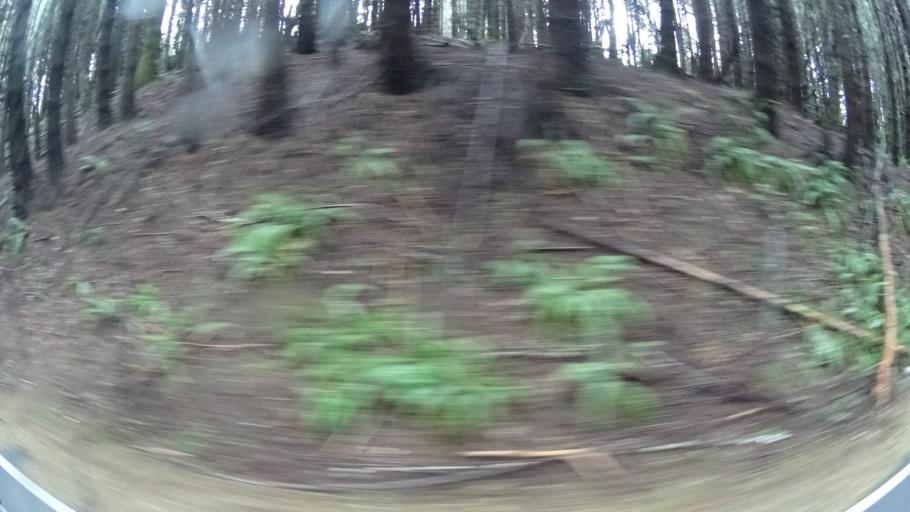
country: US
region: California
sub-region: Humboldt County
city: Westhaven-Moonstone
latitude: 41.2165
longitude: -123.9569
